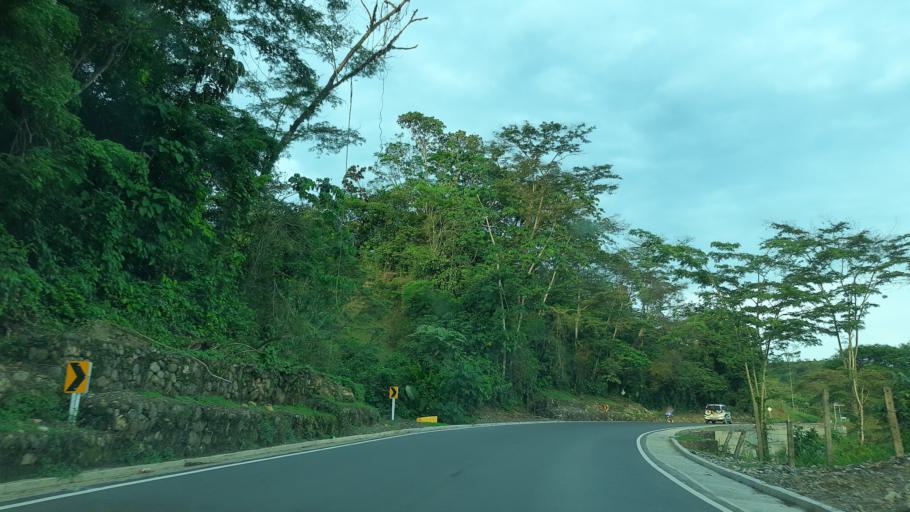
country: CO
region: Casanare
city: Sabanalarga
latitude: 4.8268
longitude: -73.0887
